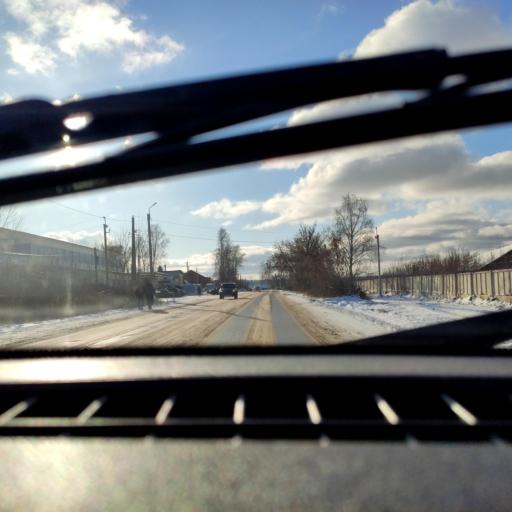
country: RU
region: Bashkortostan
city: Iglino
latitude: 54.8198
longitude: 56.3963
